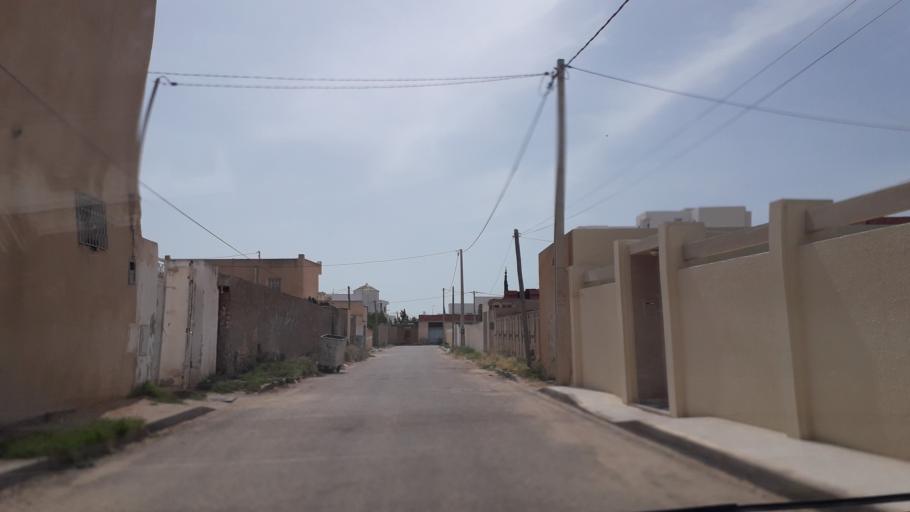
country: TN
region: Safaqis
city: Al Qarmadah
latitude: 34.8008
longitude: 10.7689
